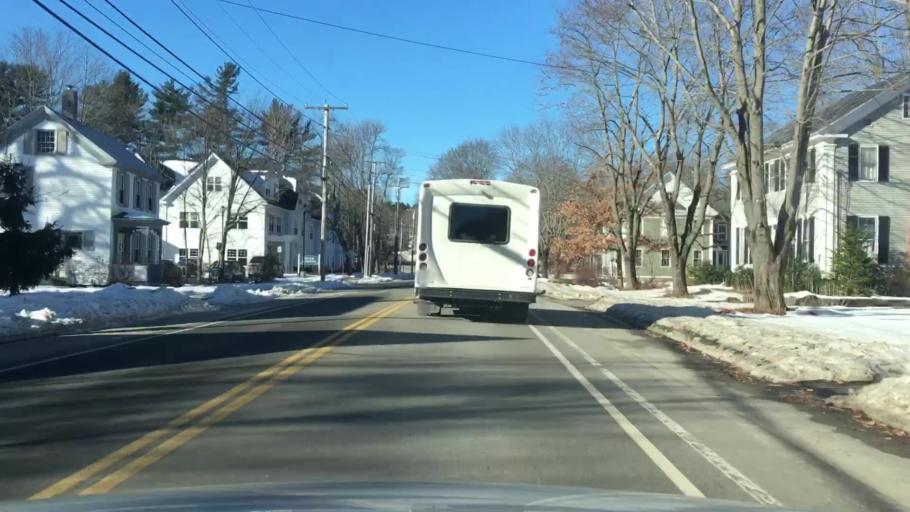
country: US
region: Maine
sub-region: Cumberland County
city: Brunswick
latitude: 43.9265
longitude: -69.9569
